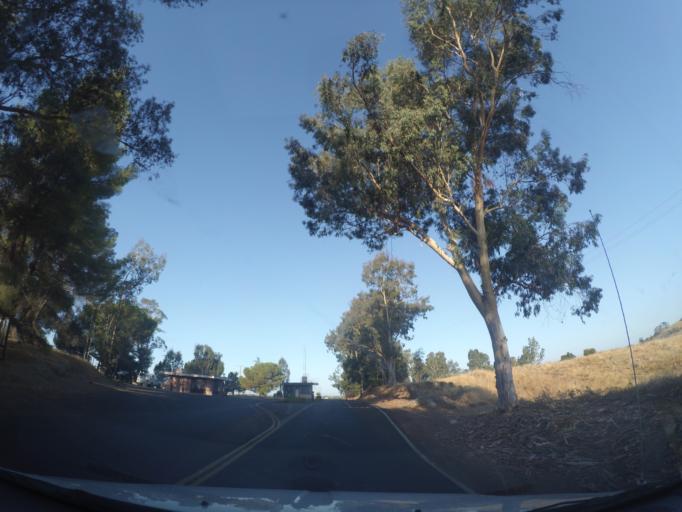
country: US
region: California
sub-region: Merced County
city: Planada
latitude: 37.5235
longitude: -120.3081
